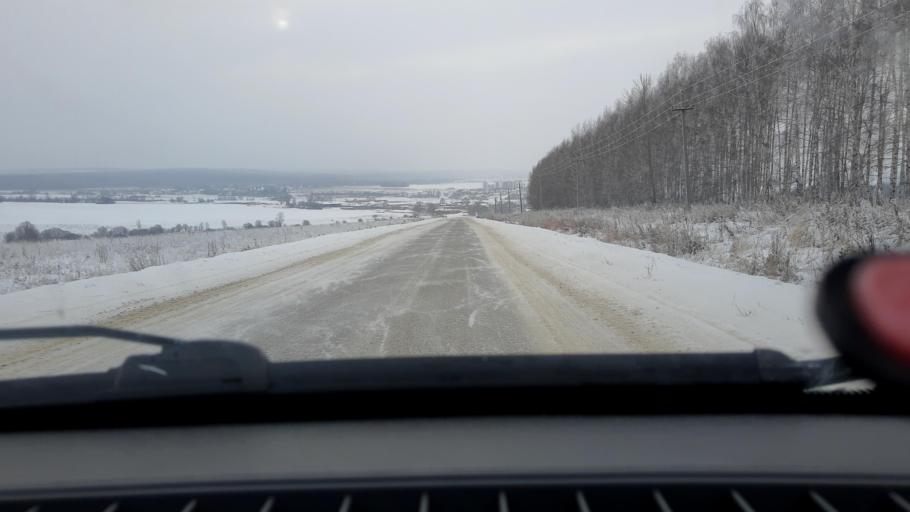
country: RU
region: Bashkortostan
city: Iglino
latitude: 54.6543
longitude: 56.4259
